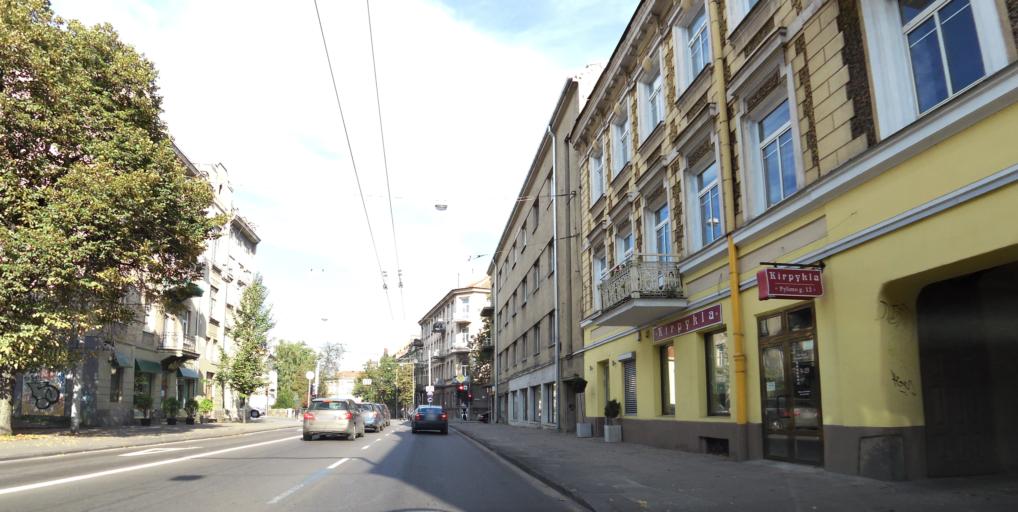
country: LT
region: Vilnius County
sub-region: Vilnius
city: Vilnius
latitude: 54.6823
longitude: 25.2773
